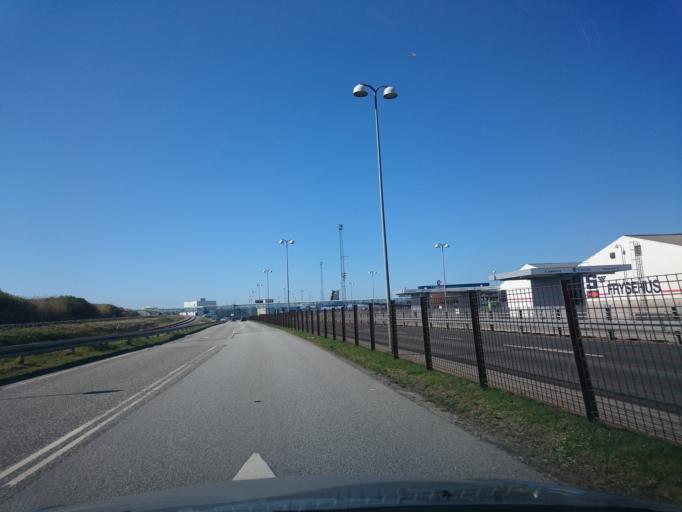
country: DK
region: North Denmark
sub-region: Hjorring Kommune
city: Hirtshals
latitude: 57.5903
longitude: 9.9712
